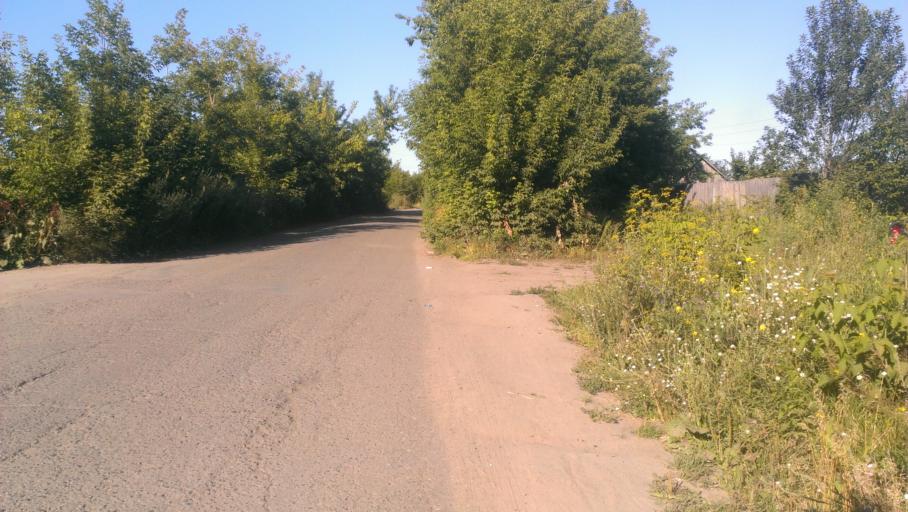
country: RU
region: Altai Krai
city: Novosilikatnyy
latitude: 53.3234
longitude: 83.6840
